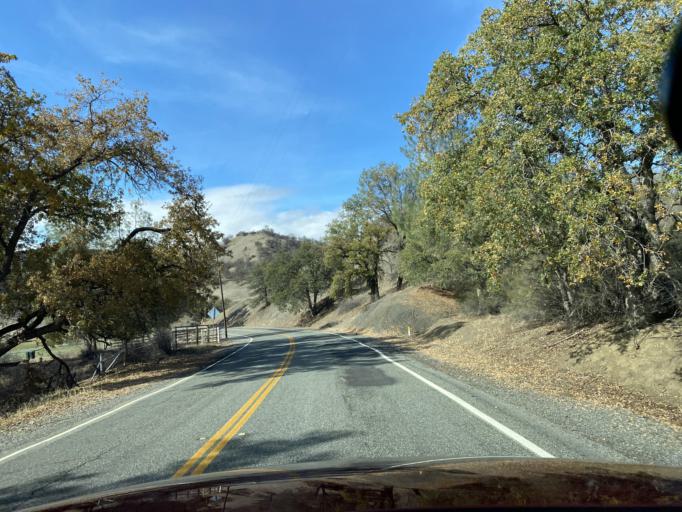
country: US
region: California
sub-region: Glenn County
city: Willows
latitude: 39.4260
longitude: -122.5253
